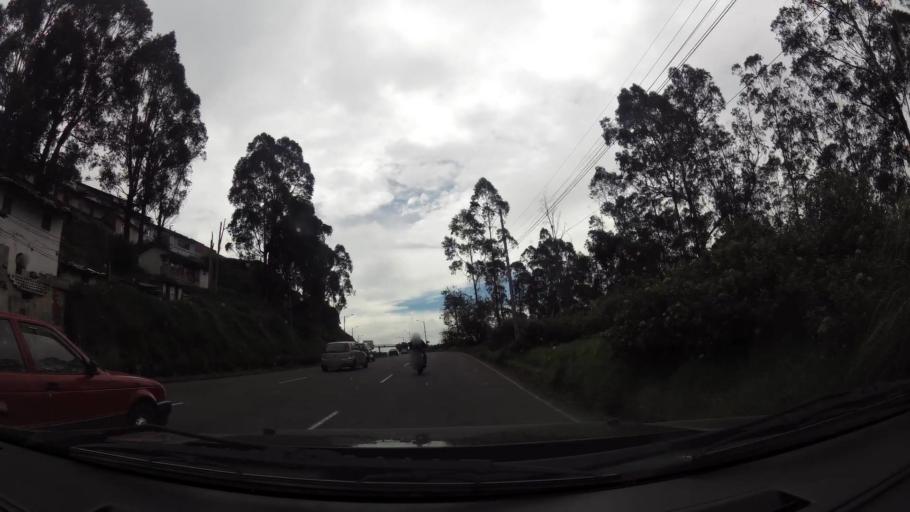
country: EC
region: Pichincha
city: Quito
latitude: -0.2191
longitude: -78.4936
